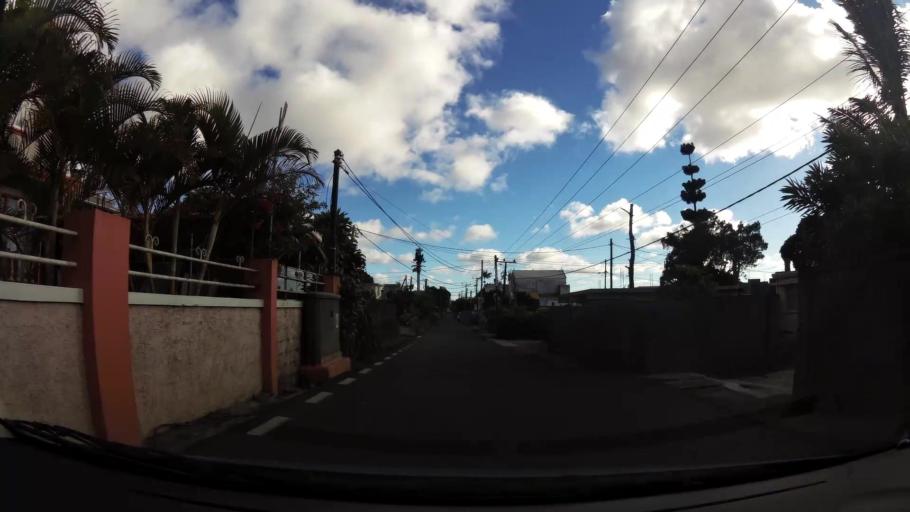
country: MU
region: Plaines Wilhems
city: Curepipe
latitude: -20.2961
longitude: 57.5136
